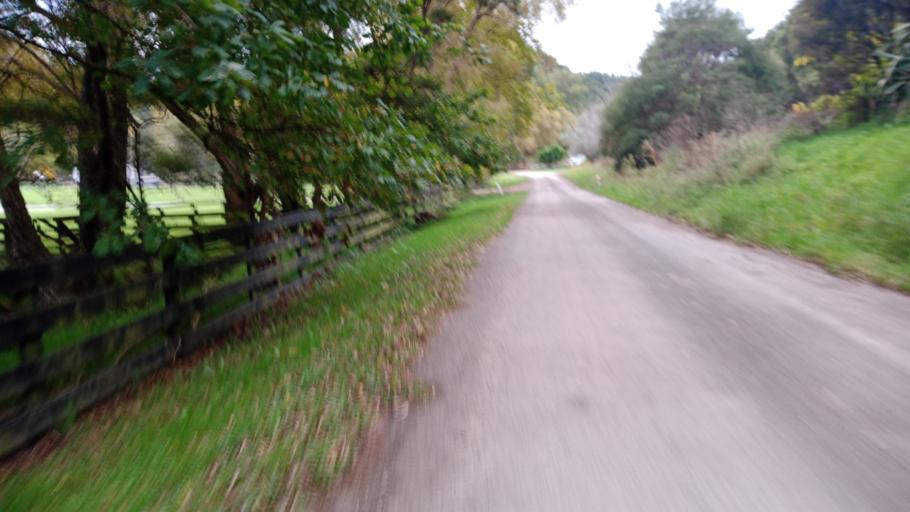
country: NZ
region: Gisborne
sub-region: Gisborne District
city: Gisborne
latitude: -38.6446
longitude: 178.0358
